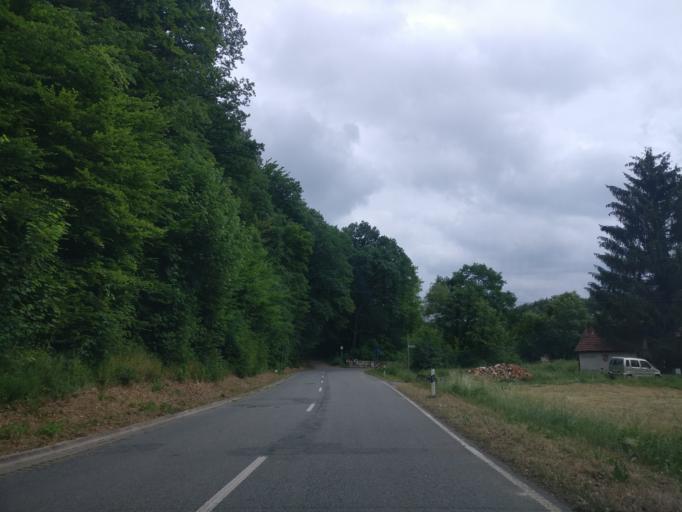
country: DE
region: Hesse
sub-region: Regierungsbezirk Kassel
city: Fuldatal
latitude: 51.3923
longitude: 9.5607
